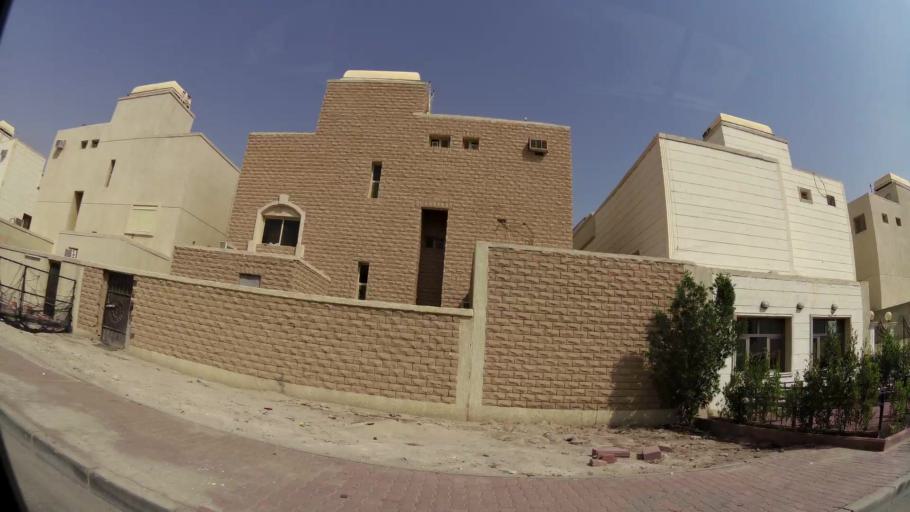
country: KW
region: Muhafazat al Jahra'
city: Al Jahra'
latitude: 29.3218
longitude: 47.7222
